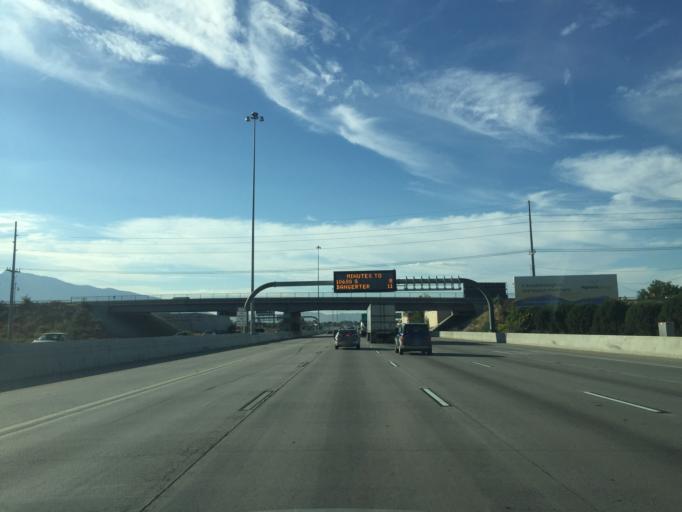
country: US
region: Utah
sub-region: Salt Lake County
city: Centerfield
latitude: 40.6881
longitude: -111.9032
